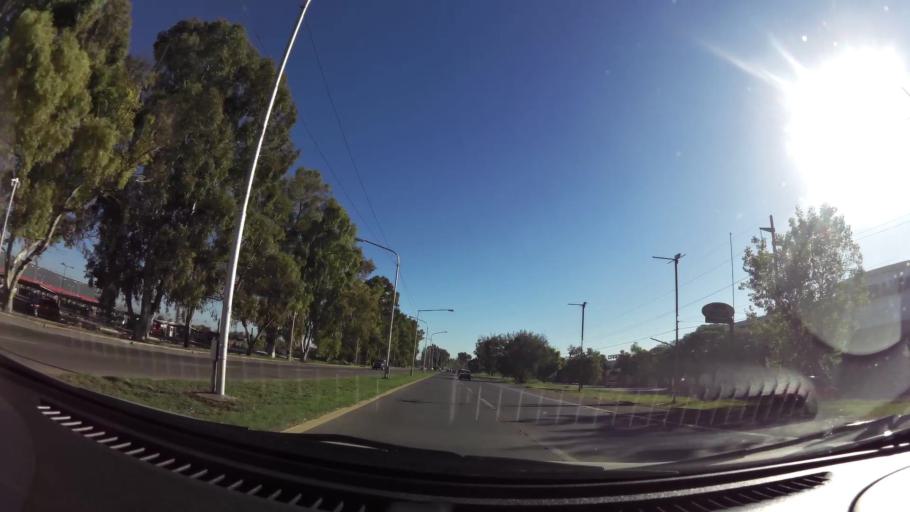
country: AR
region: Mendoza
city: Las Heras
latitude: -32.8539
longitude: -68.8060
